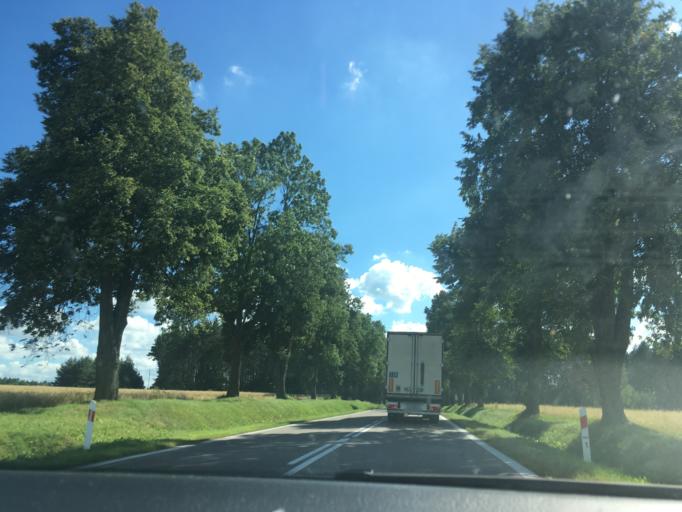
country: PL
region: Podlasie
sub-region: Powiat sokolski
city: Suchowola
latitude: 53.6011
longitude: 23.1135
